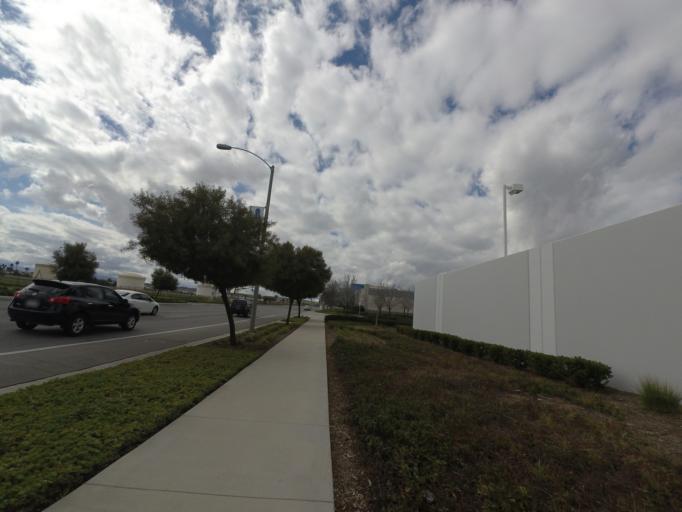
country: US
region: California
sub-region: Riverside County
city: March Air Force Base
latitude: 33.9103
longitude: -117.2649
